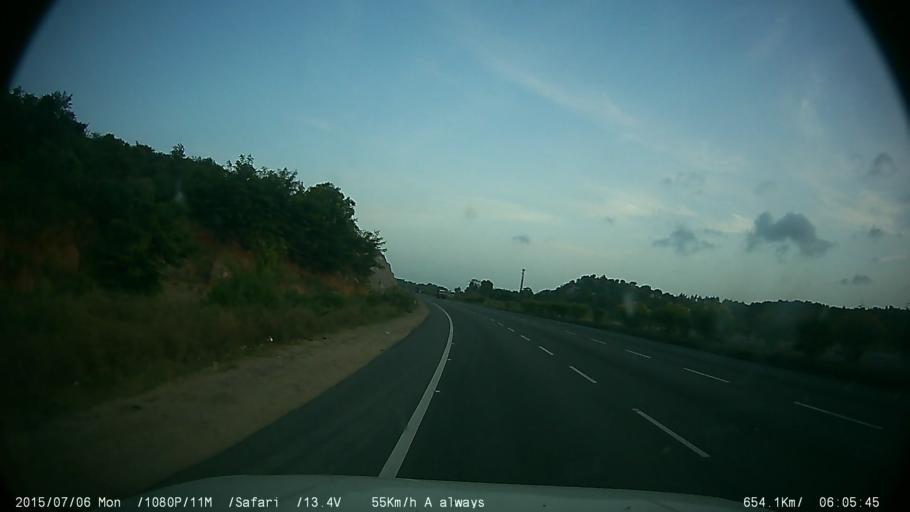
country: IN
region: Tamil Nadu
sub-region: Krishnagiri
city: Krishnagiri
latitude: 12.6266
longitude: 78.0791
